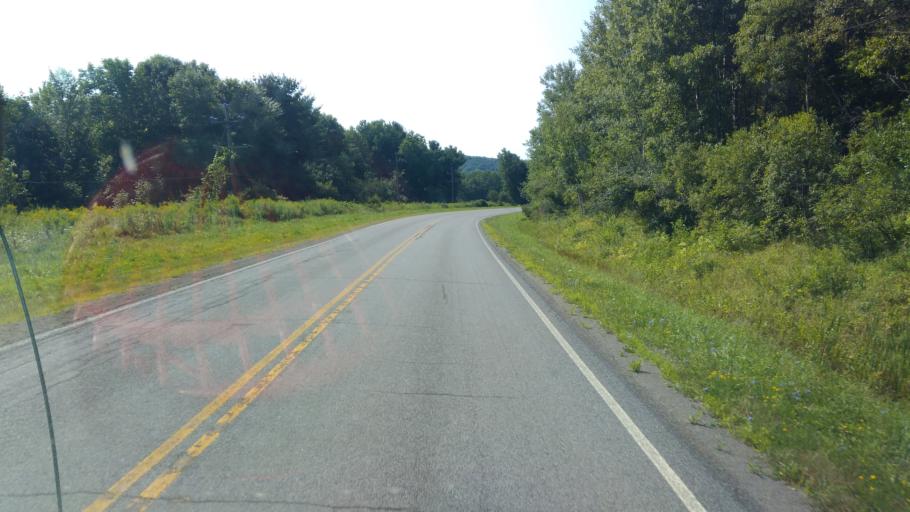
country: US
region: New York
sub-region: Allegany County
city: Friendship
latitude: 42.1410
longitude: -78.1499
